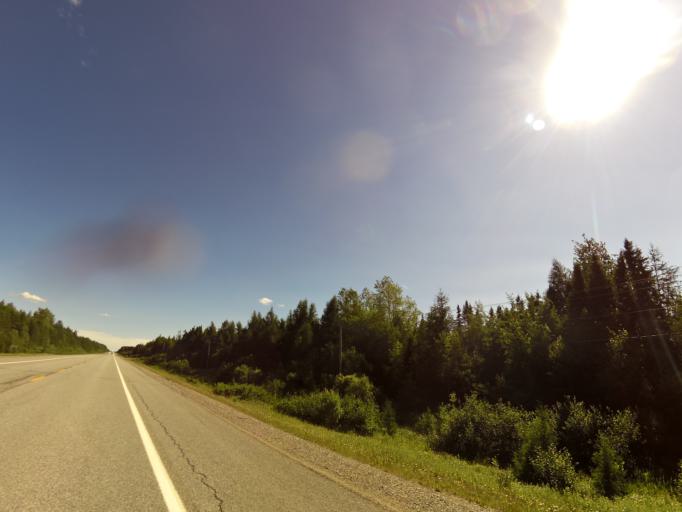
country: CA
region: Quebec
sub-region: Abitibi-Temiscamingue
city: Senneterre
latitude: 47.9774
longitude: -77.3609
